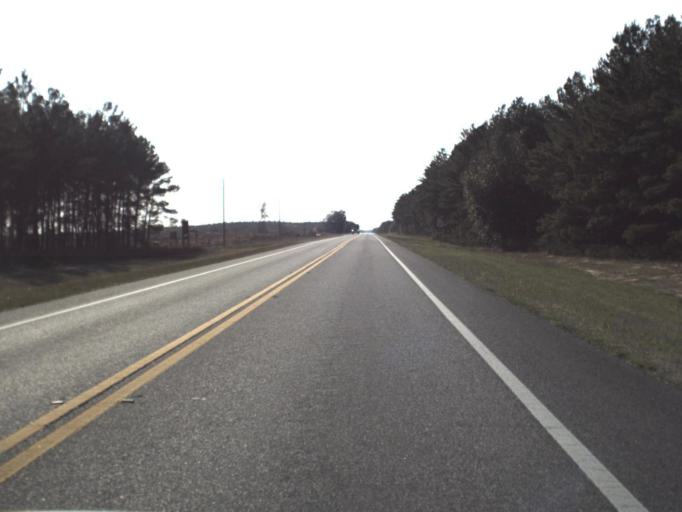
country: US
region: Florida
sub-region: Bay County
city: Youngstown
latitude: 30.4278
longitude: -85.6088
